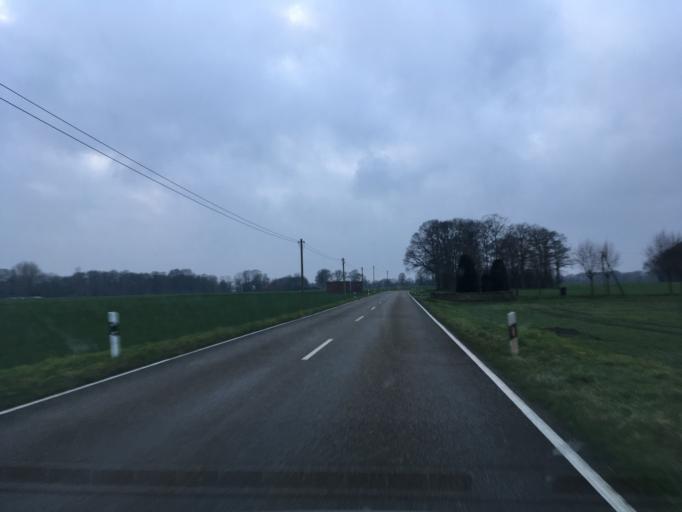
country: DE
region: North Rhine-Westphalia
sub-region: Regierungsbezirk Munster
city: Heek
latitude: 52.1754
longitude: 7.0875
